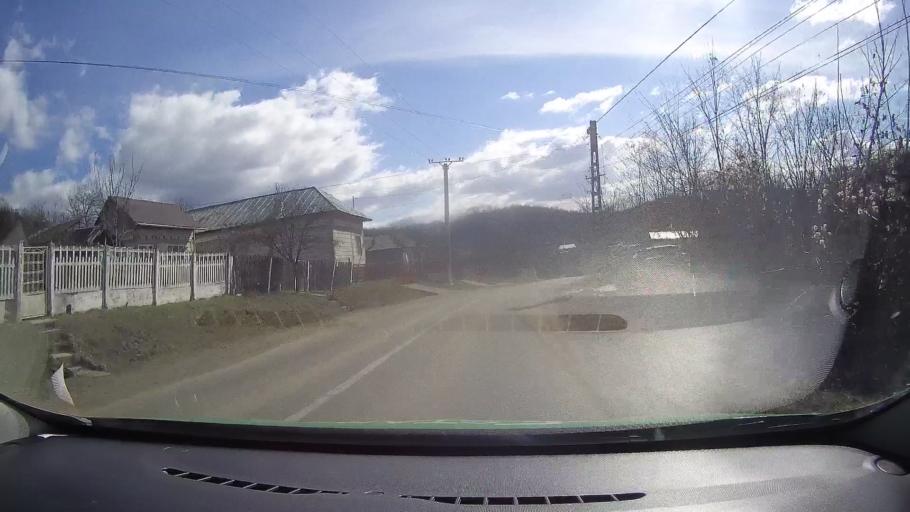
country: RO
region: Dambovita
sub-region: Comuna Glodeni
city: Laculete
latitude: 45.0233
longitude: 25.4327
